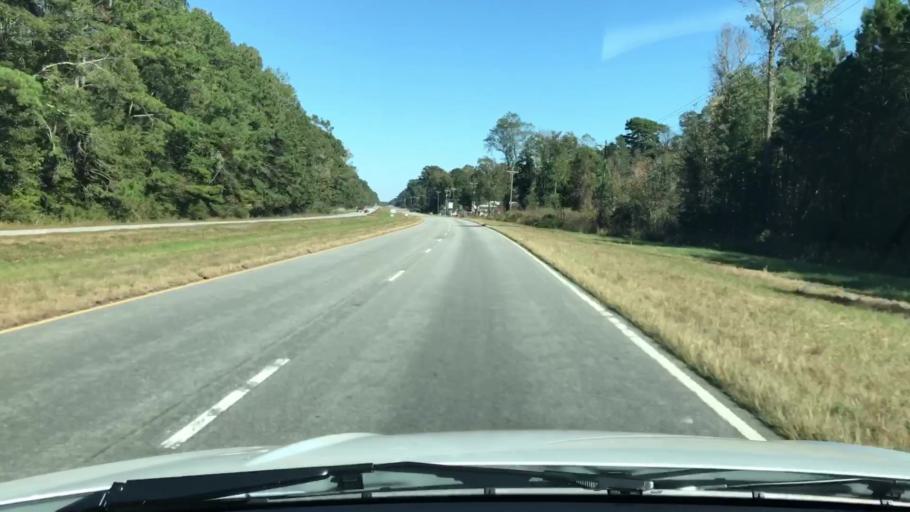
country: US
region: South Carolina
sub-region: Charleston County
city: Ravenel
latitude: 32.7555
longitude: -80.3275
